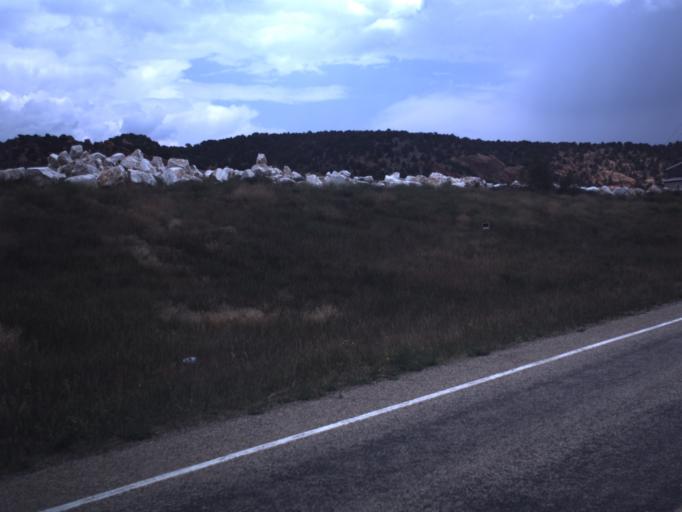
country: US
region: Utah
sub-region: Duchesne County
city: Duchesne
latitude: 40.4237
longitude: -110.7975
